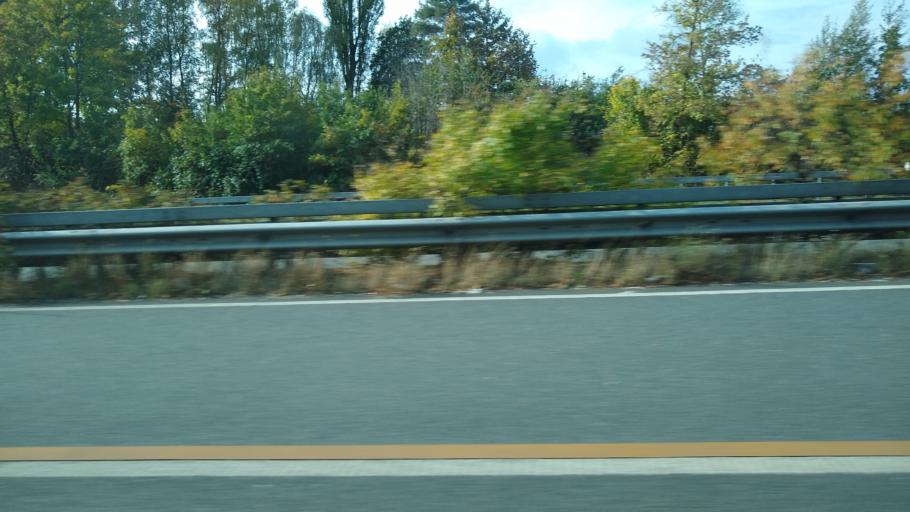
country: DE
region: Lower Saxony
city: Oldenburg
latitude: 53.1541
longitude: 8.1943
